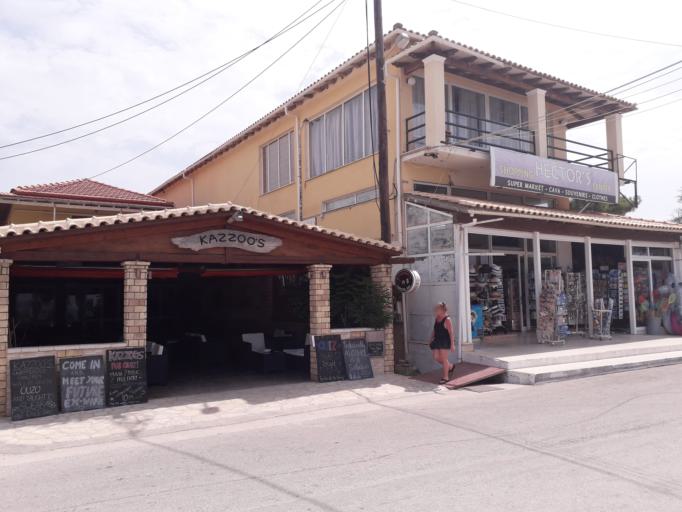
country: GR
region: Ionian Islands
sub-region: Nomos Kerkyras
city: Perivoli
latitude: 39.4263
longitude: 19.9444
